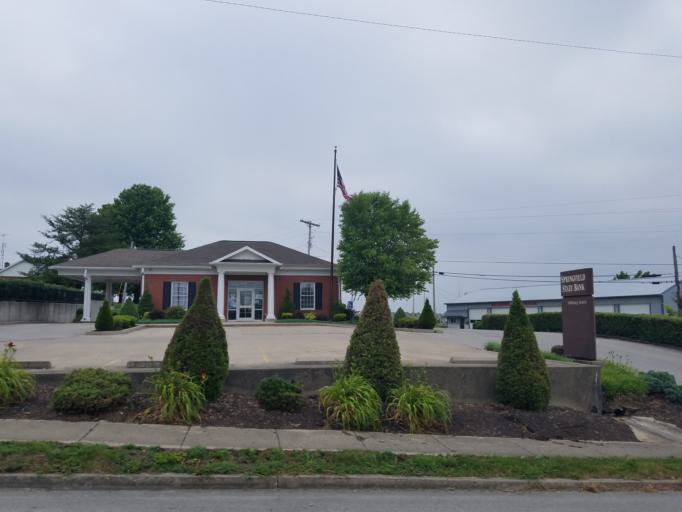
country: US
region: Kentucky
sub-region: Washington County
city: Springfield
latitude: 37.8078
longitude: -85.1242
